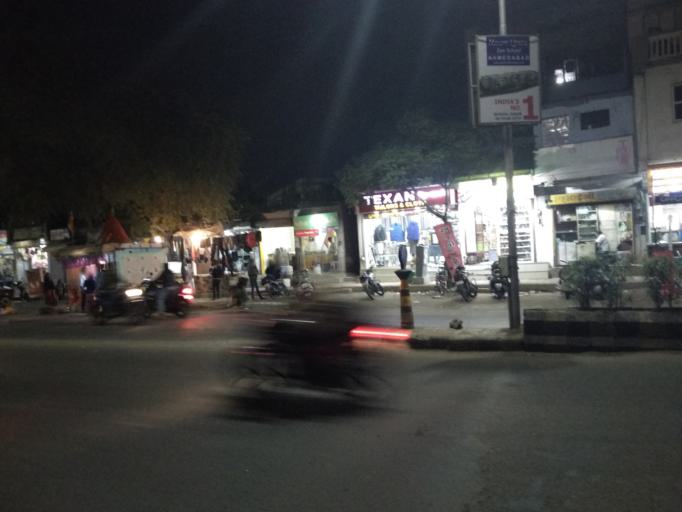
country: IN
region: Gujarat
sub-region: Ahmadabad
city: Naroda
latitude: 23.0550
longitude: 72.6188
